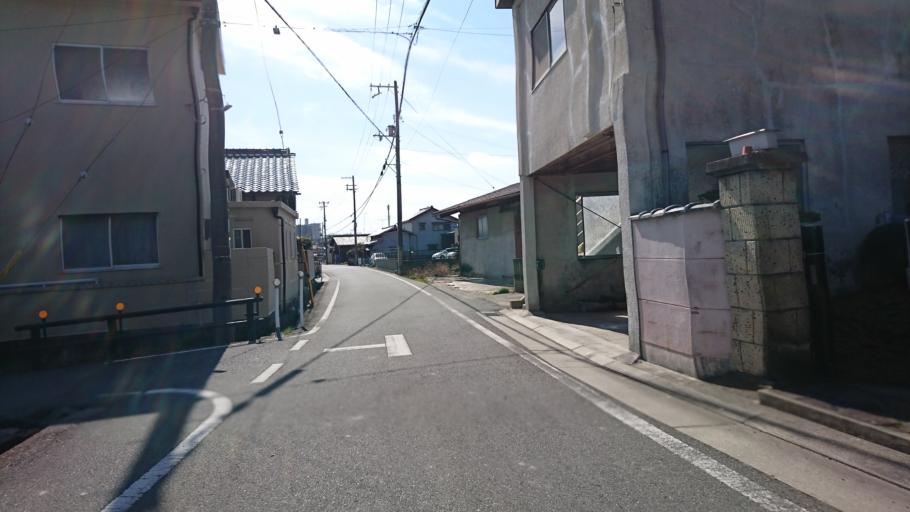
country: JP
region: Hyogo
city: Kakogawacho-honmachi
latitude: 34.7977
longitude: 134.8082
